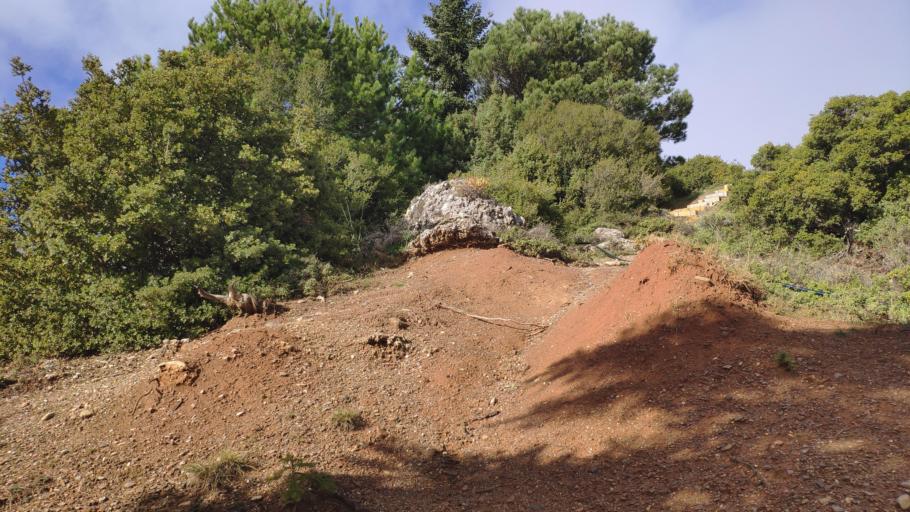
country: GR
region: West Greece
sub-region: Nomos Achaias
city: Aiyira
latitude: 38.0566
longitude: 22.4406
